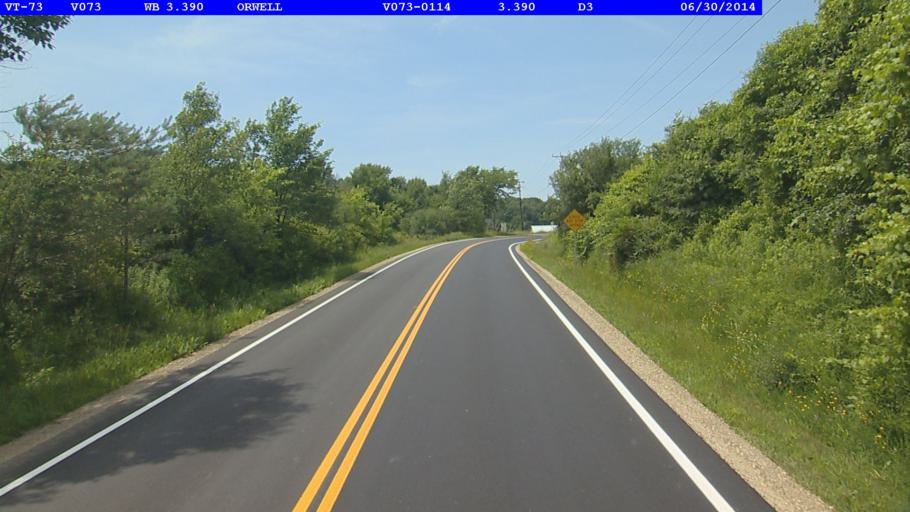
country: US
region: Vermont
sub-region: Rutland County
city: Brandon
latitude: 43.7988
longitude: -73.2421
